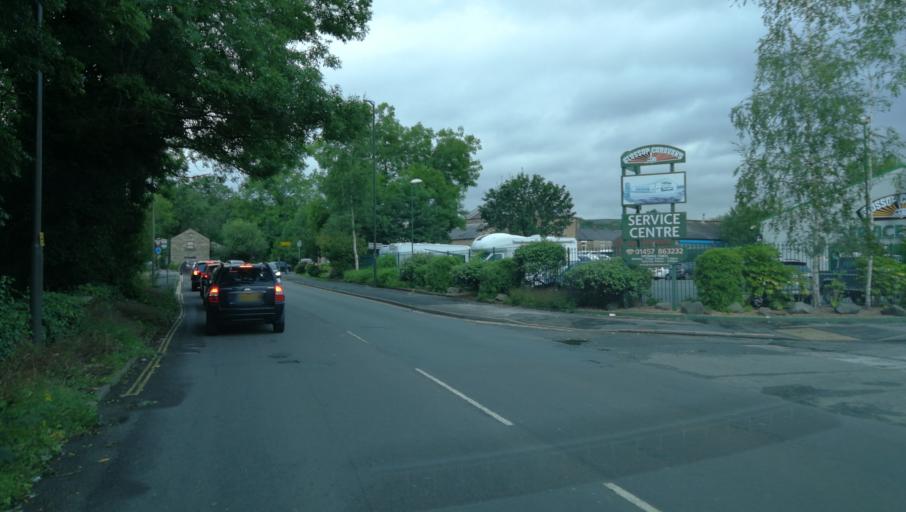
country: GB
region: England
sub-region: Borough of Tameside
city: Longdendale
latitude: 53.4583
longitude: -1.9863
